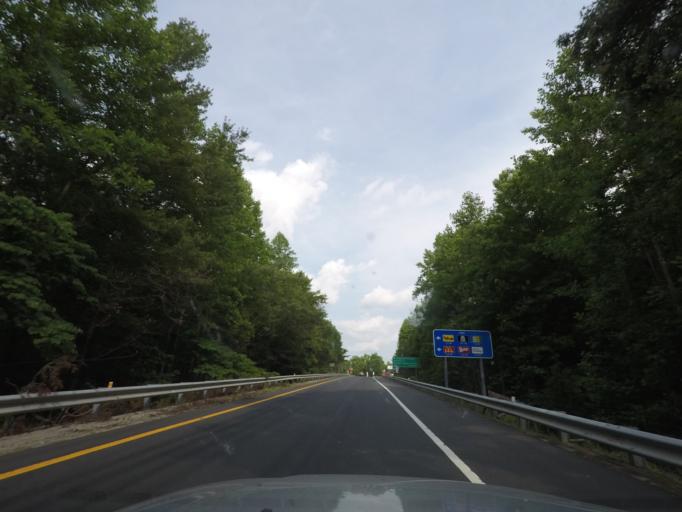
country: US
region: Virginia
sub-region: Prince Edward County
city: Farmville
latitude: 37.2687
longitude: -78.4078
